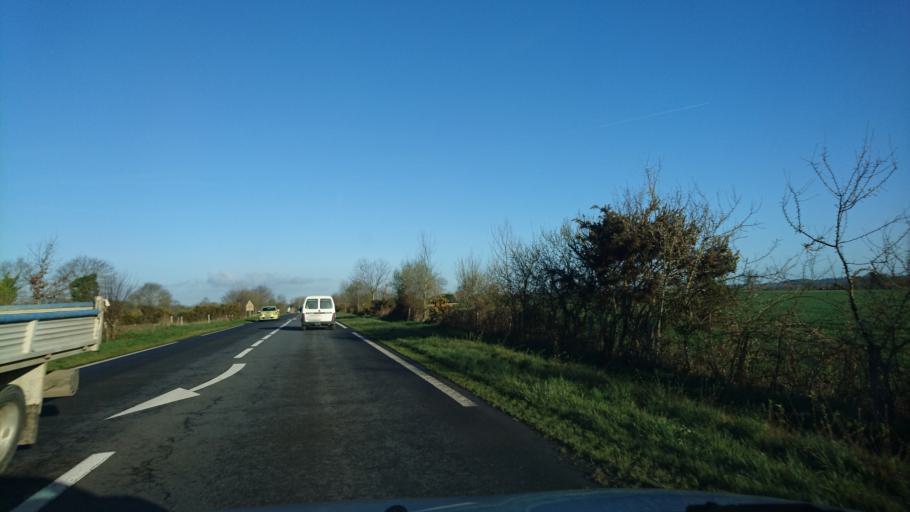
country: FR
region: Brittany
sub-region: Departement d'Ille-et-Vilaine
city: La Boussac
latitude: 48.5052
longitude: -1.6398
